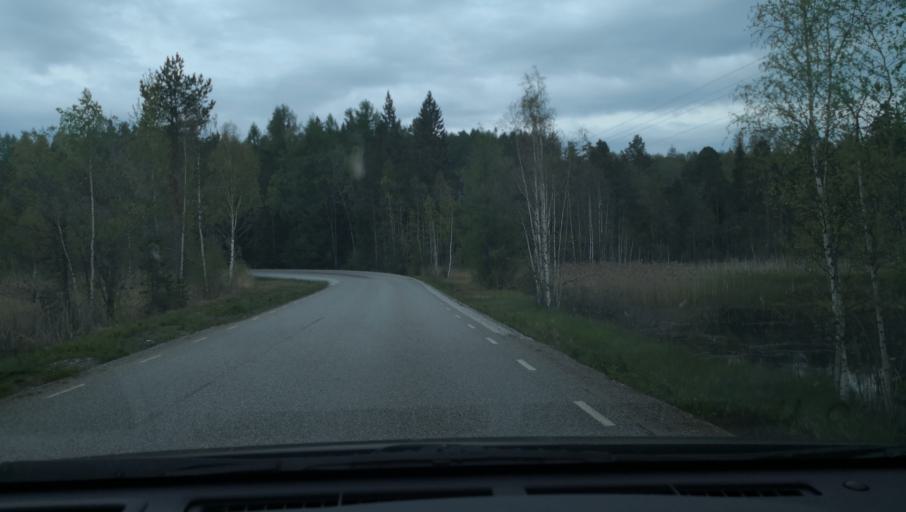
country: SE
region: Vaestmanland
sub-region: Skinnskattebergs Kommun
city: Skinnskatteberg
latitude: 59.8312
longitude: 15.5773
